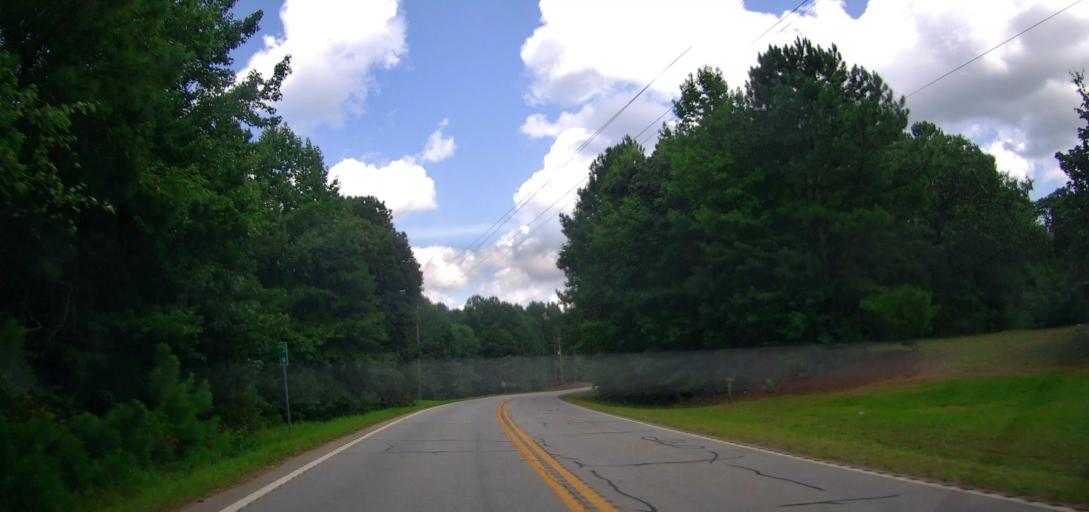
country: US
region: Georgia
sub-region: Heard County
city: Franklin
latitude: 33.3570
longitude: -85.1970
